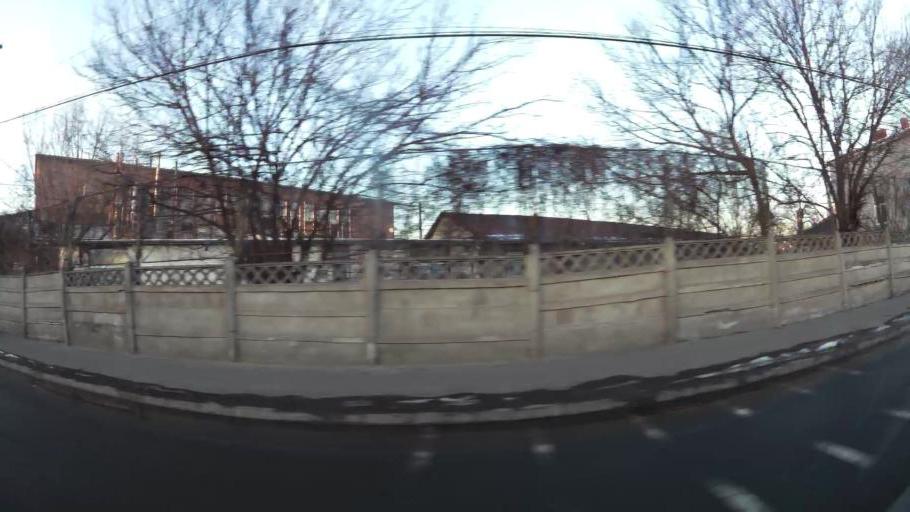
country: RO
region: Ilfov
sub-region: Comuna Fundeni-Dobroesti
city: Fundeni
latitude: 44.4512
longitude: 26.1381
